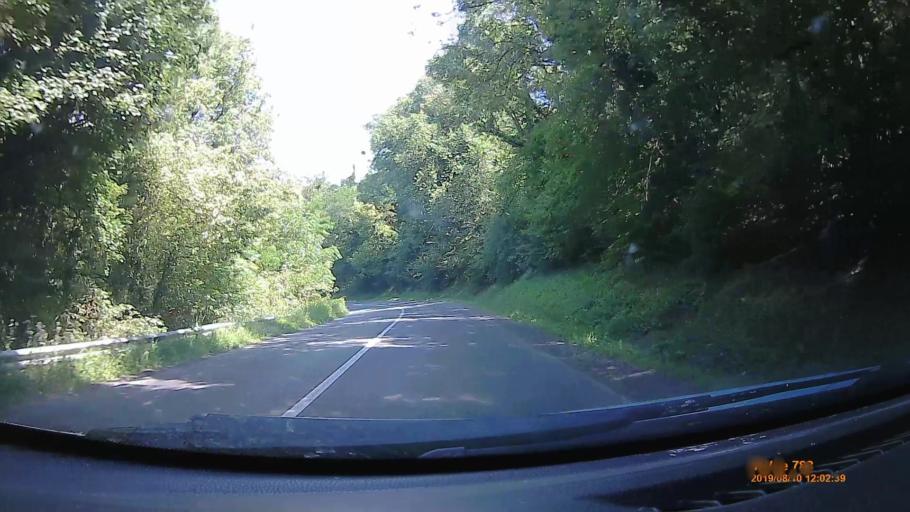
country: HU
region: Somogy
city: Somogyvar
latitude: 46.5750
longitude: 17.6484
